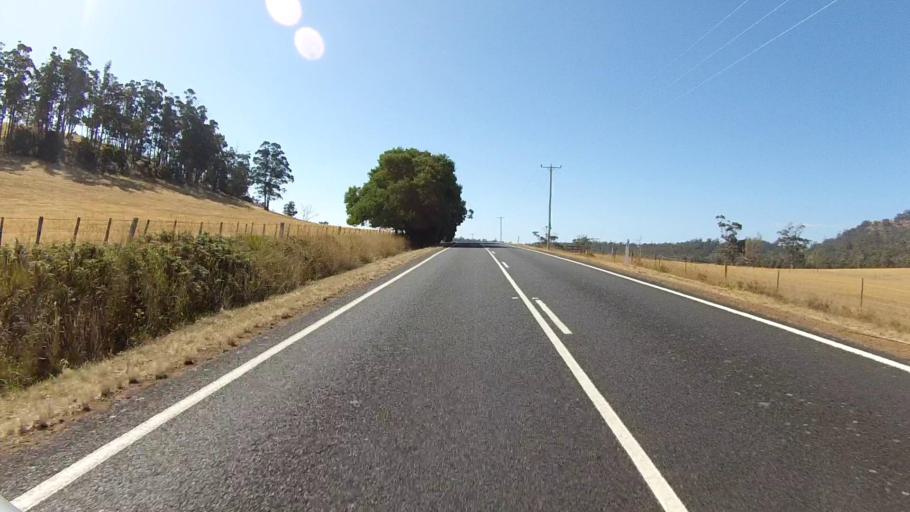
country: AU
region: Tasmania
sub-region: Sorell
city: Sorell
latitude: -42.4242
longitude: 147.9338
